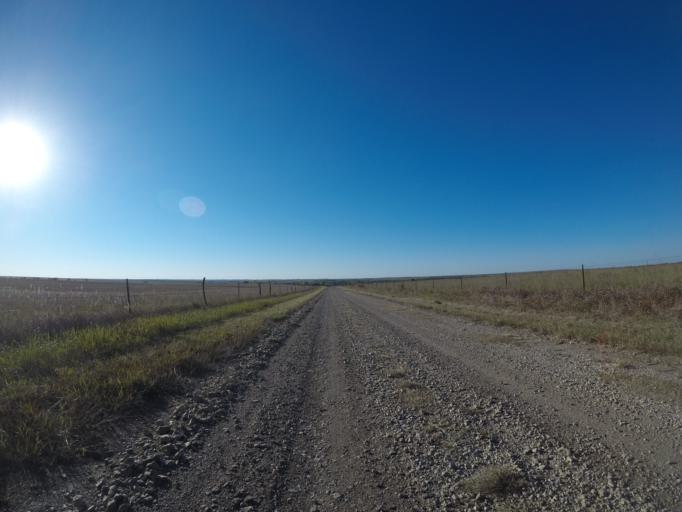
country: US
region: Kansas
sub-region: Wabaunsee County
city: Alma
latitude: 38.9359
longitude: -96.4641
